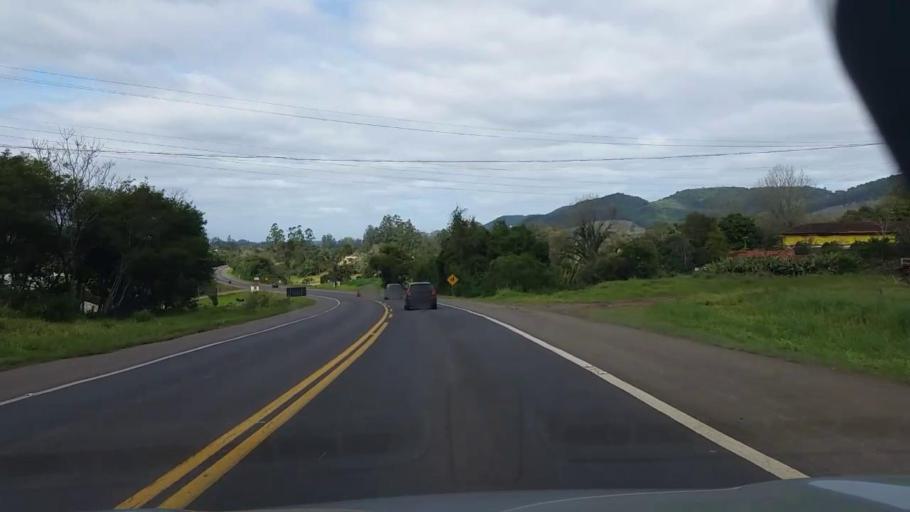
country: BR
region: Rio Grande do Sul
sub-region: Arroio Do Meio
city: Arroio do Meio
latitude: -29.3403
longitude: -52.0781
